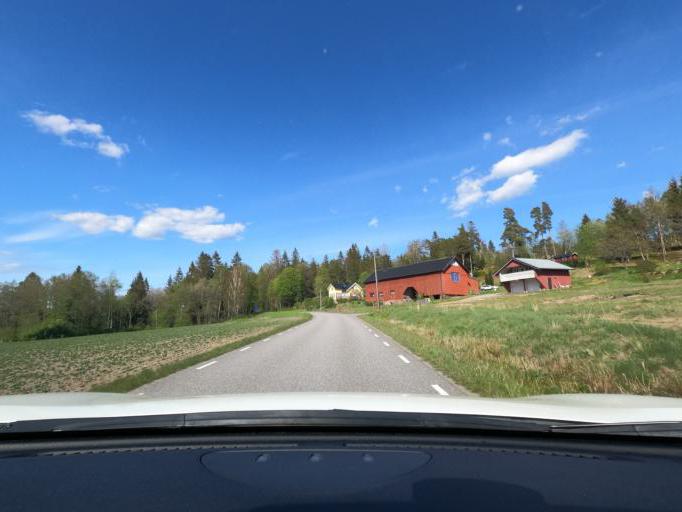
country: SE
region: Vaestra Goetaland
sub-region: Harryda Kommun
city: Ravlanda
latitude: 57.6141
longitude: 12.4941
